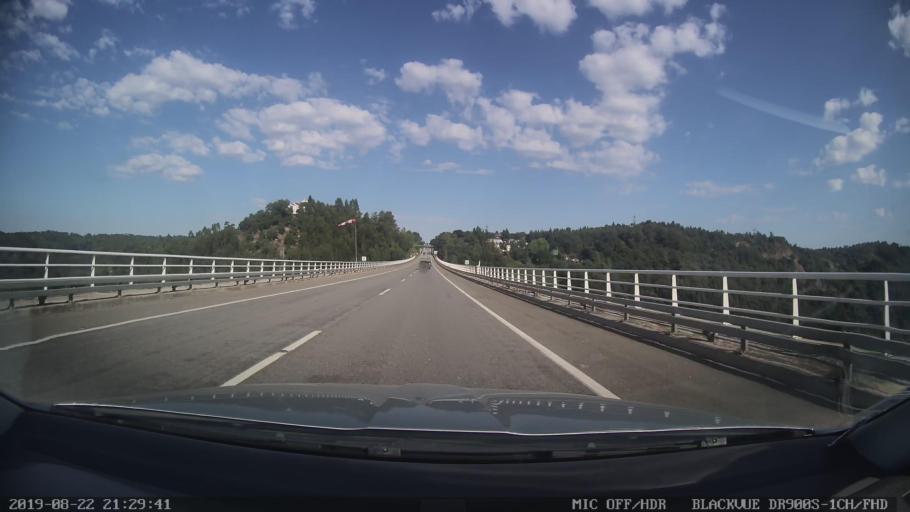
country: PT
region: Leiria
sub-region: Pedrogao Grande
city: Pedrogao Grande
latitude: 39.9040
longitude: -8.1391
